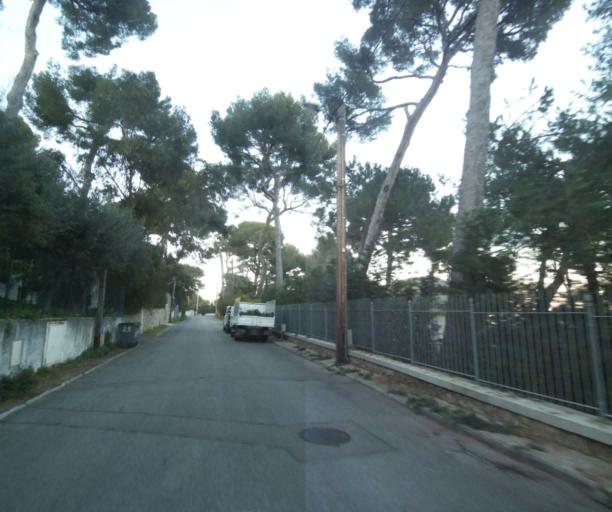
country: FR
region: Provence-Alpes-Cote d'Azur
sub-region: Departement des Alpes-Maritimes
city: Antibes
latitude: 43.5645
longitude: 7.1344
